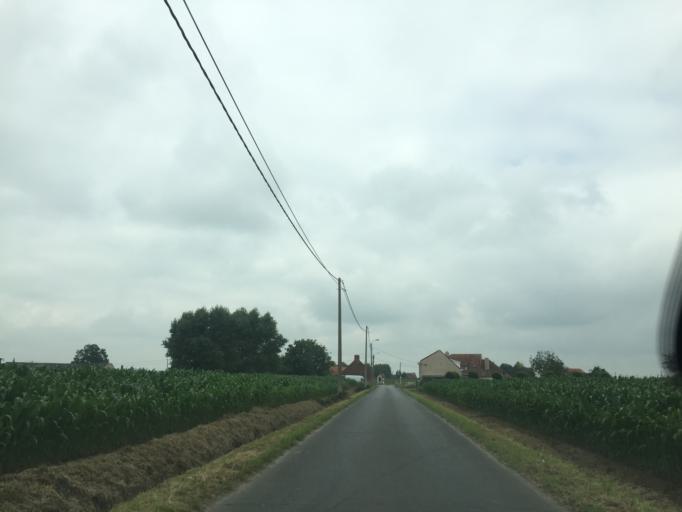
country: BE
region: Flanders
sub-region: Provincie West-Vlaanderen
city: Kortemark
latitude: 51.0064
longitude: 3.0250
